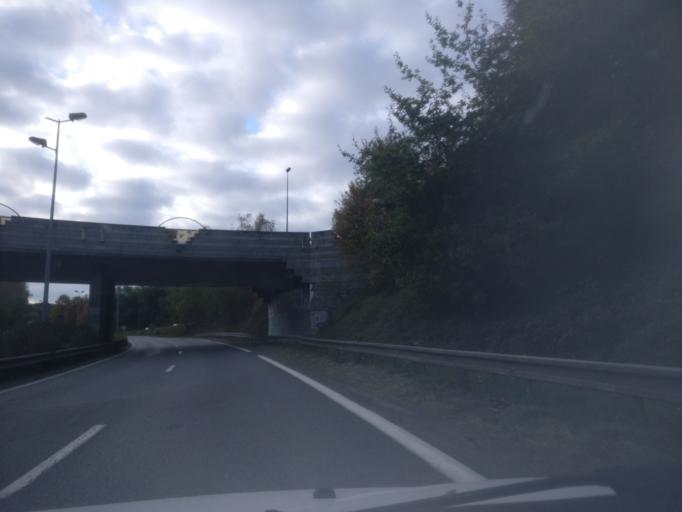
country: FR
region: Pays de la Loire
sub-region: Departement de la Loire-Atlantique
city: La Chapelle-sur-Erdre
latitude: 47.2599
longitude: -1.5569
